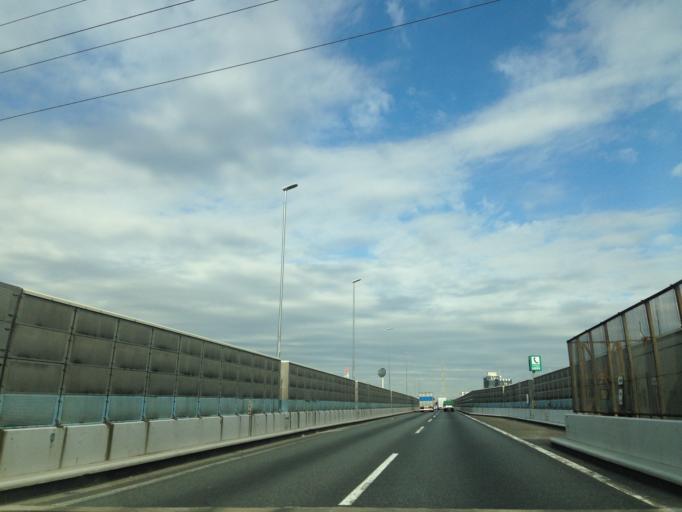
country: JP
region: Saitama
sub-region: Kawaguchi-shi
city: Hatogaya-honcho
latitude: 35.8206
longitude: 139.7599
